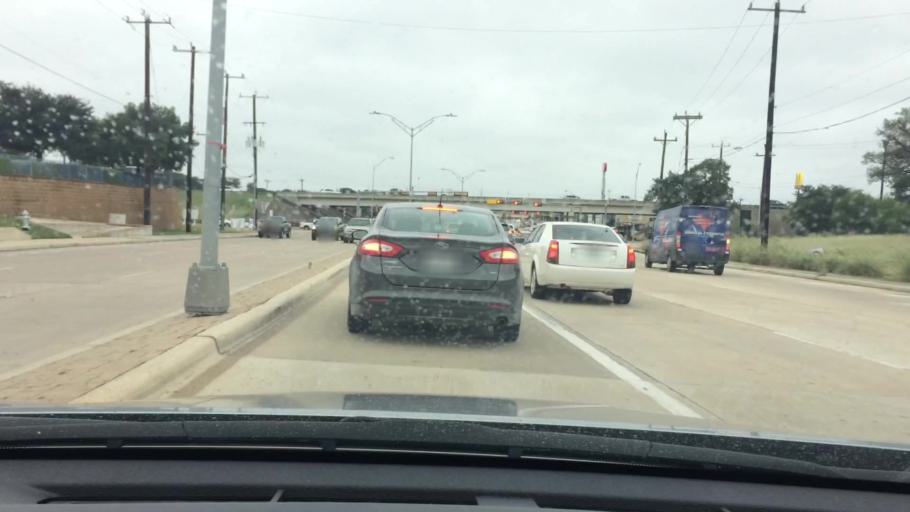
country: US
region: Texas
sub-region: Bexar County
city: Hollywood Park
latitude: 29.6024
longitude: -98.4186
